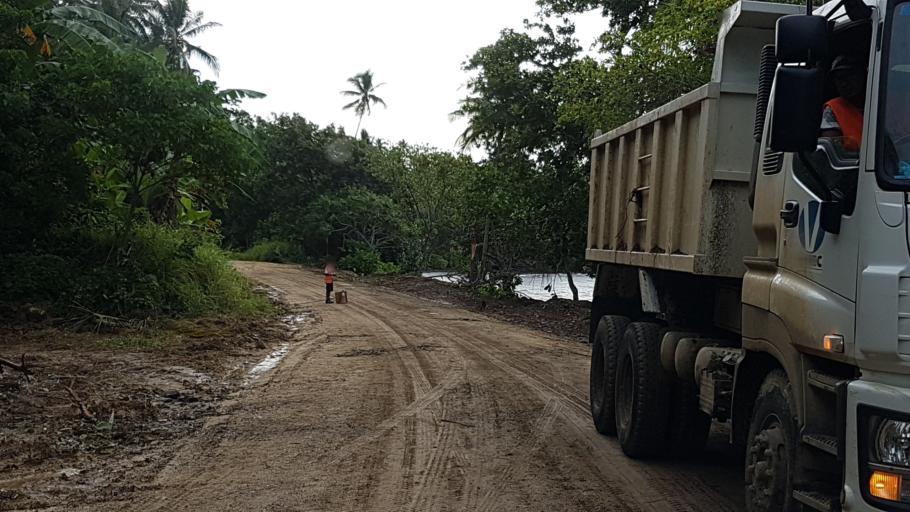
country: PG
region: Milne Bay
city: Alotau
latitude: -10.2983
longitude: 150.7624
